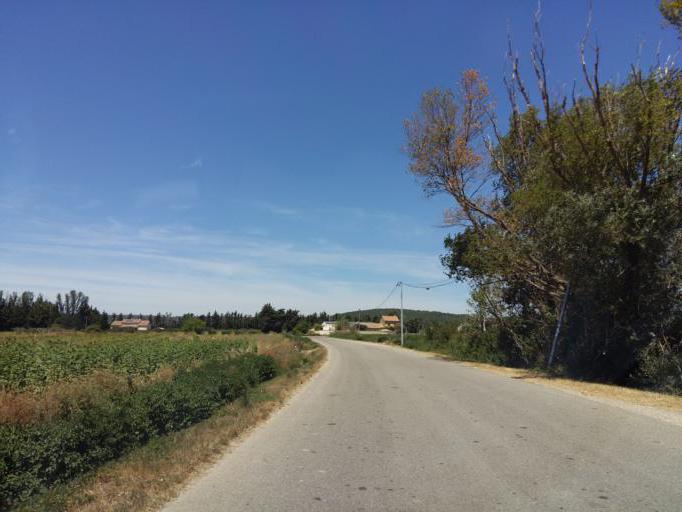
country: FR
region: Provence-Alpes-Cote d'Azur
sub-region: Departement du Vaucluse
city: Piolenc
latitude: 44.1696
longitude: 4.7561
